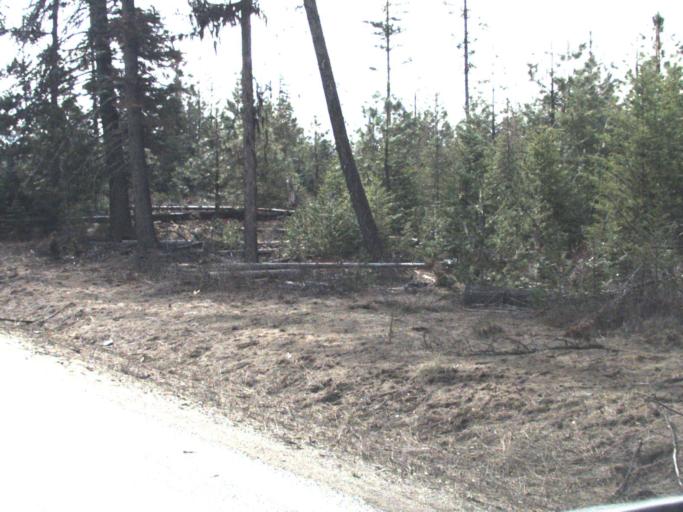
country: US
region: Washington
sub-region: Pend Oreille County
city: Newport
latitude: 48.2834
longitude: -117.2693
